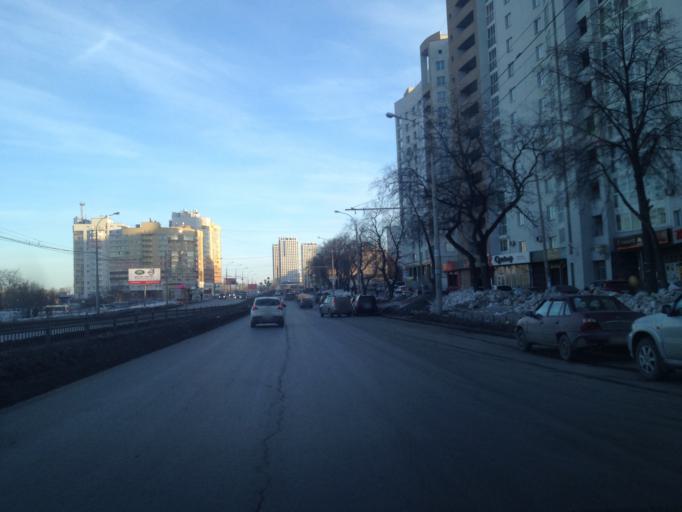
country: RU
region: Sverdlovsk
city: Yekaterinburg
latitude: 56.7855
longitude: 60.6501
